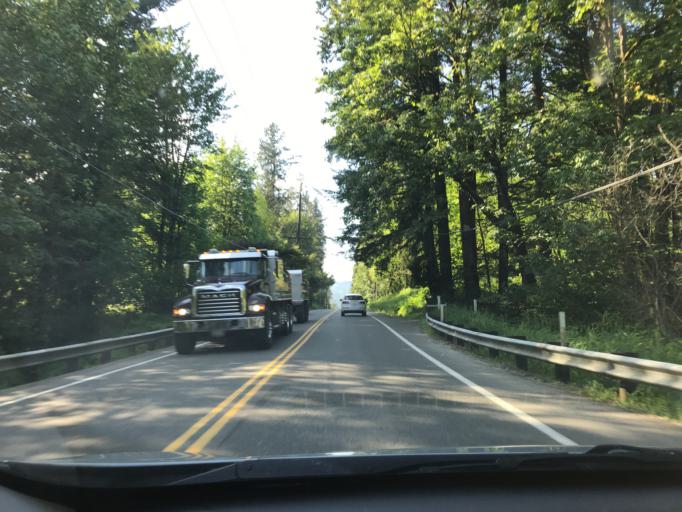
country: US
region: Washington
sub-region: King County
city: Mirrormont
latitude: 47.4635
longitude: -122.0140
